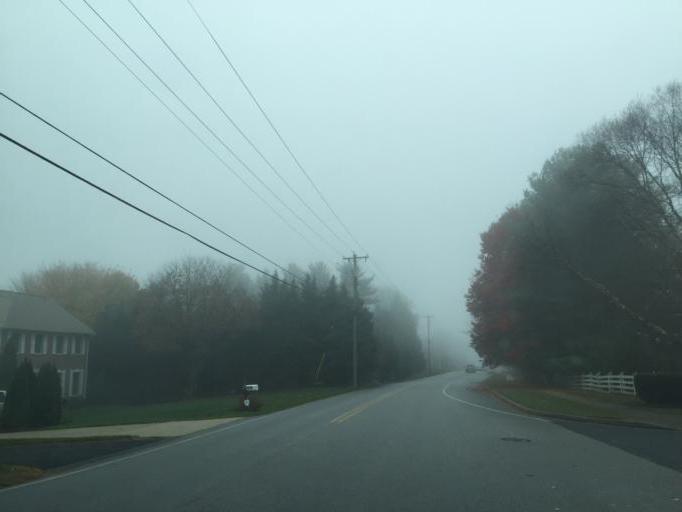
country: US
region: Maryland
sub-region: Howard County
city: Columbia
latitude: 39.2527
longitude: -76.8530
